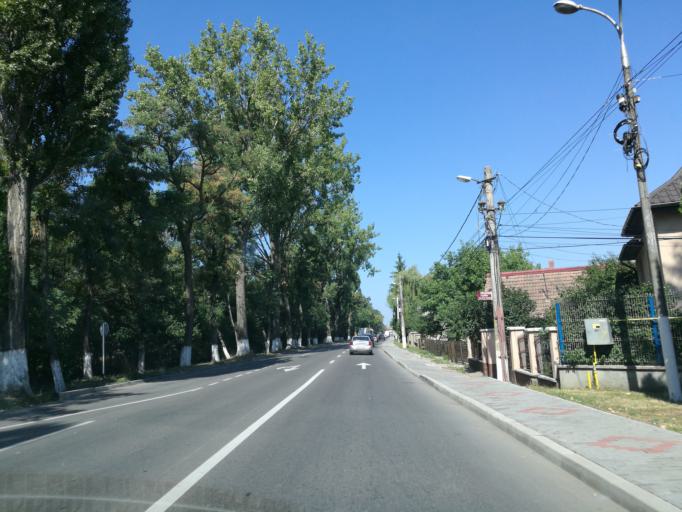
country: RO
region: Suceava
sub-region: Municipiul Suceava
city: Radauti
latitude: 47.8336
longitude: 25.9316
